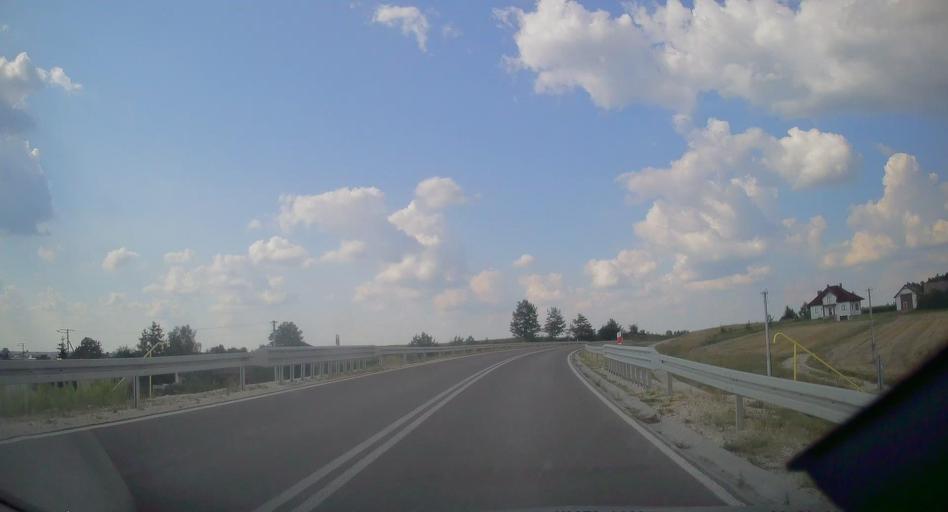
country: PL
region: Swietokrzyskie
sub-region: Powiat kielecki
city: Lopuszno
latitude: 50.9755
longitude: 20.2472
